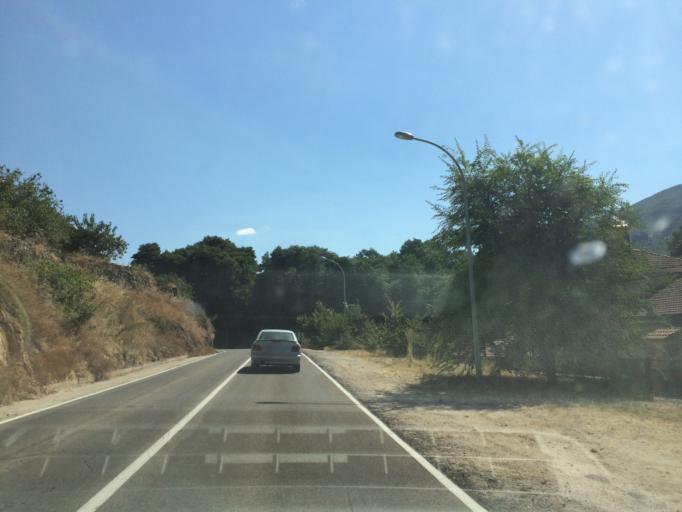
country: ES
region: Extremadura
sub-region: Provincia de Caceres
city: Cabezuela del Valle
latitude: 40.1994
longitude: -5.8013
